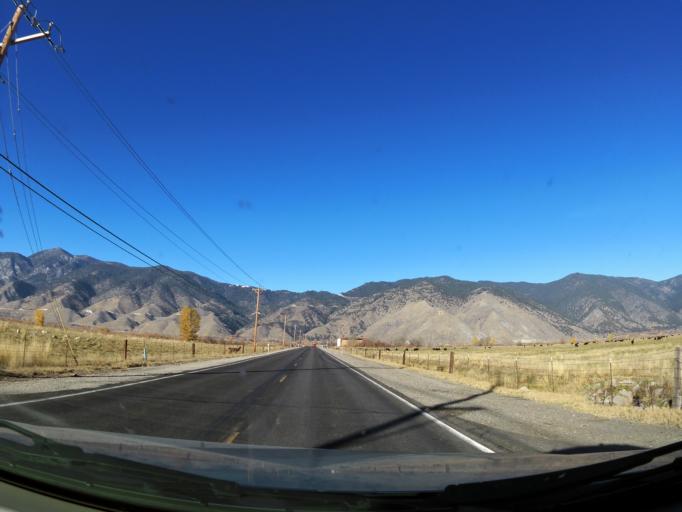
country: US
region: Nevada
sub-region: Douglas County
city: Minden
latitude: 38.9708
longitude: -119.7958
